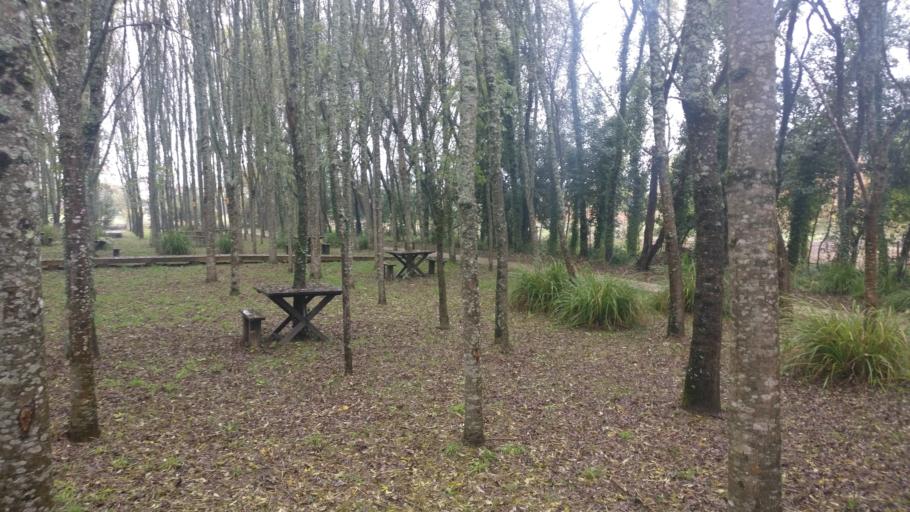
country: PT
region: Viseu
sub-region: Mortagua
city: Mortagua
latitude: 40.3947
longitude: -8.2273
